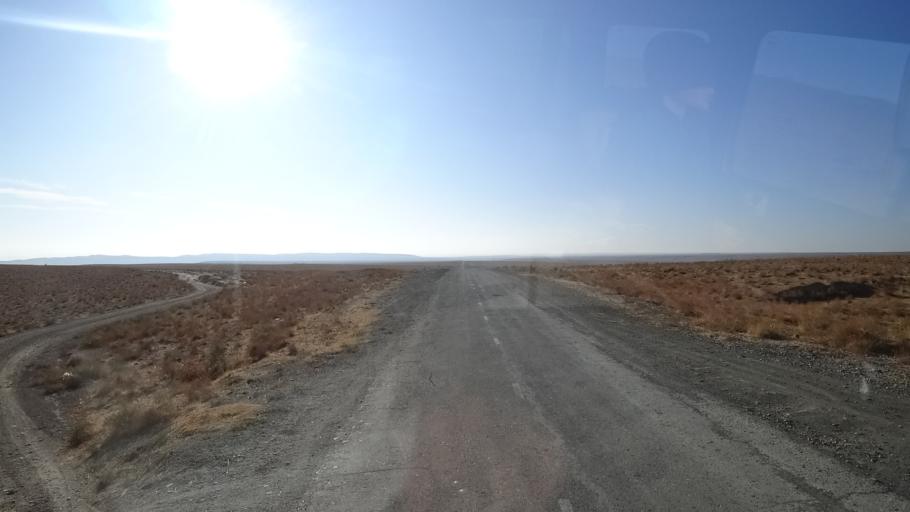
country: UZ
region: Navoiy
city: Karmana Shahri
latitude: 40.2810
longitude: 65.5648
